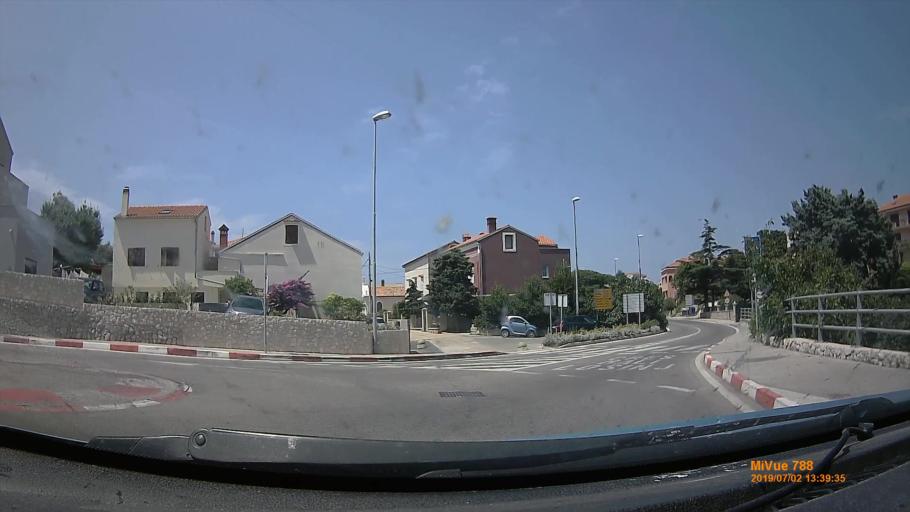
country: HR
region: Primorsko-Goranska
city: Mali Losinj
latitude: 44.5277
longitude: 14.4775
